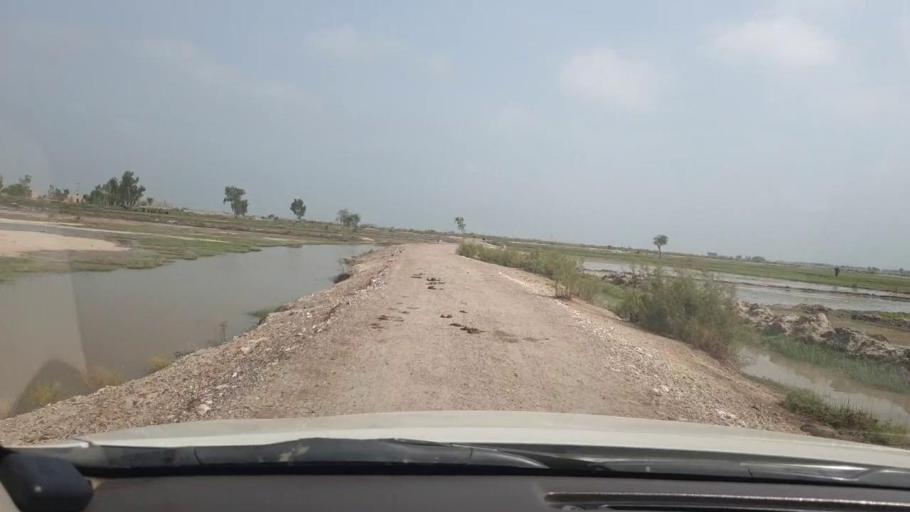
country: PK
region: Sindh
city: Shikarpur
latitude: 28.0224
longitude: 68.5901
